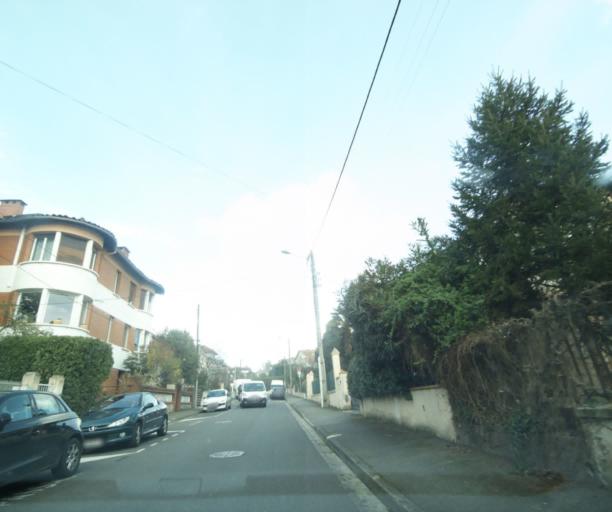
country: FR
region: Midi-Pyrenees
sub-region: Departement de la Haute-Garonne
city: Toulouse
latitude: 43.5864
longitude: 1.4730
